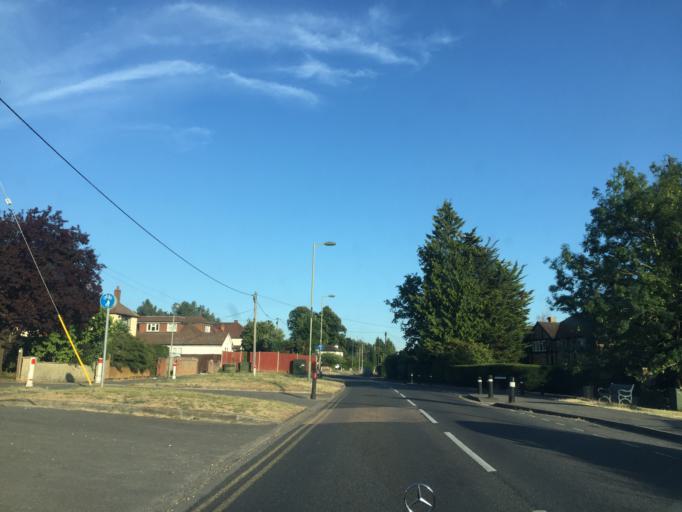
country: GB
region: England
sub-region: Surrey
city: Frimley
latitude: 51.3077
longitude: -0.7314
